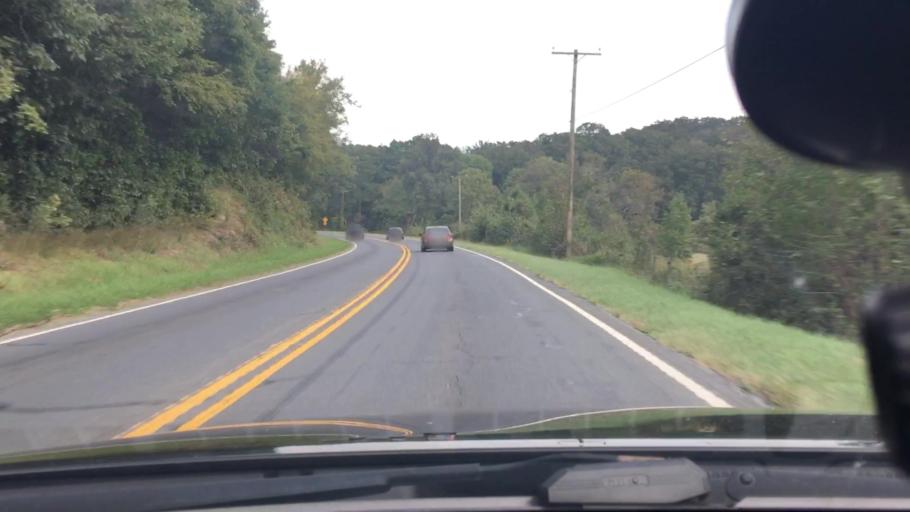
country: US
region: North Carolina
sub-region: Stanly County
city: Albemarle
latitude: 35.3194
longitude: -80.1216
